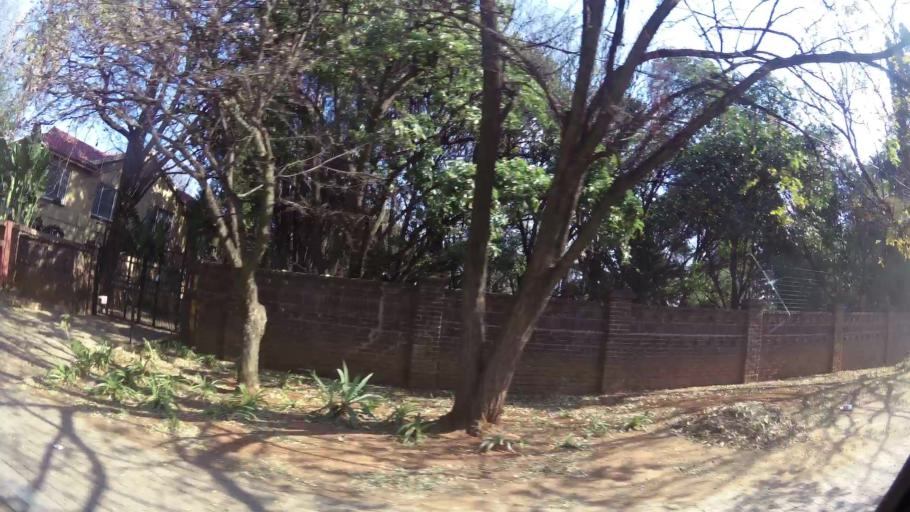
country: ZA
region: Gauteng
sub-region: Ekurhuleni Metropolitan Municipality
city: Boksburg
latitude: -26.1939
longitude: 28.2858
